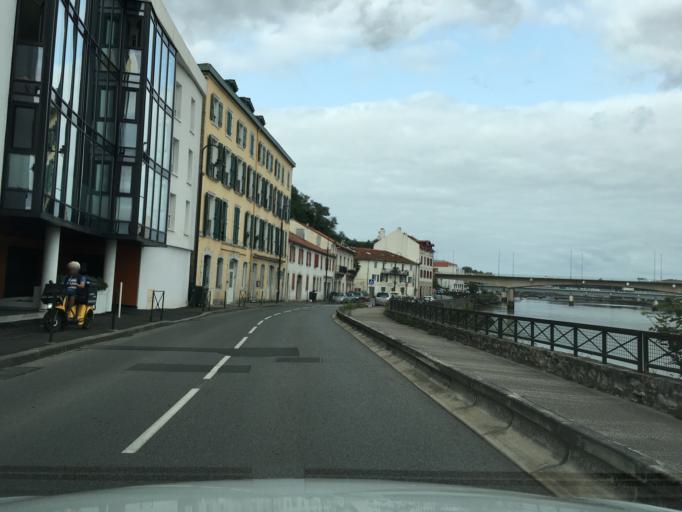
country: FR
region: Aquitaine
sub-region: Departement des Pyrenees-Atlantiques
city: Bayonne
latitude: 43.4854
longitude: -1.4598
